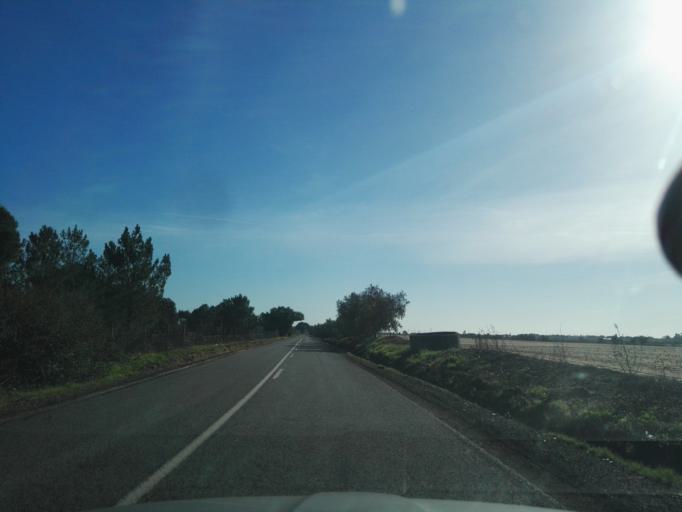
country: PT
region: Setubal
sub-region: Alcochete
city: Alcochete
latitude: 38.7331
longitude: -8.9247
